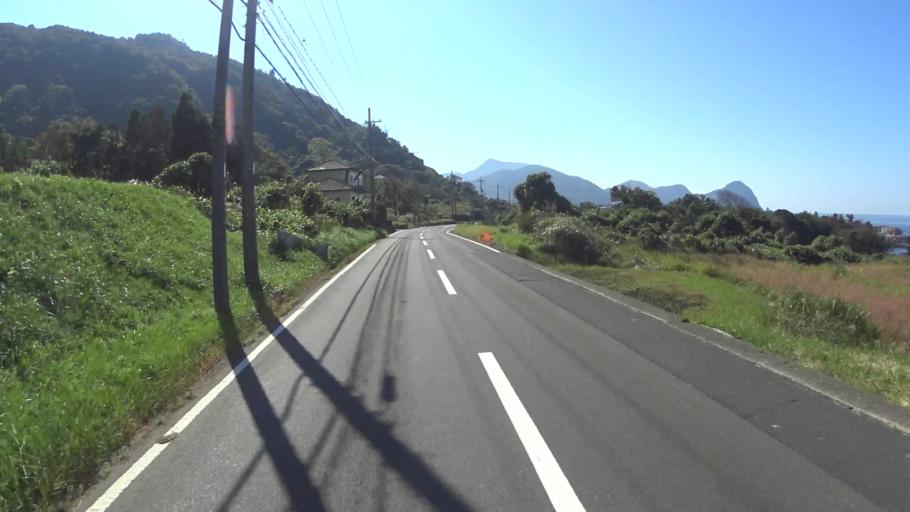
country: JP
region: Kyoto
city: Miyazu
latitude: 35.7631
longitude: 135.1867
